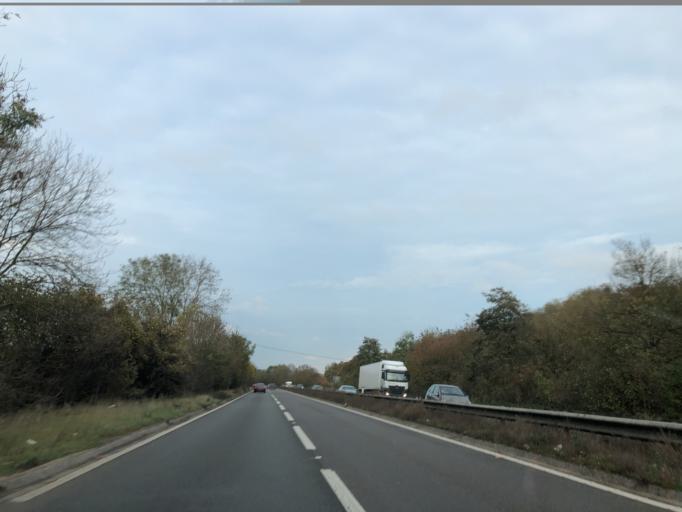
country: GB
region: England
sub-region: Royal Borough of Windsor and Maidenhead
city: Bisham
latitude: 51.5579
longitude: -0.7699
